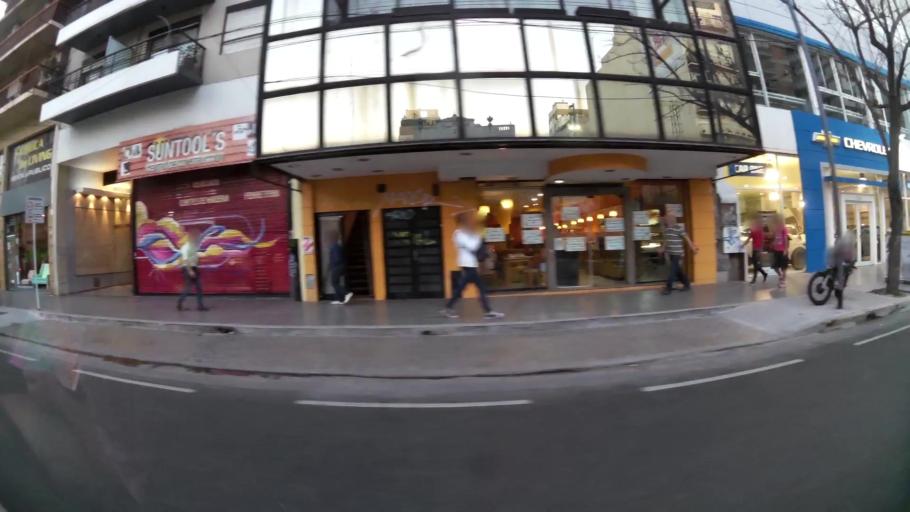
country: AR
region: Buenos Aires F.D.
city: Colegiales
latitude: -34.5528
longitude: -58.4657
